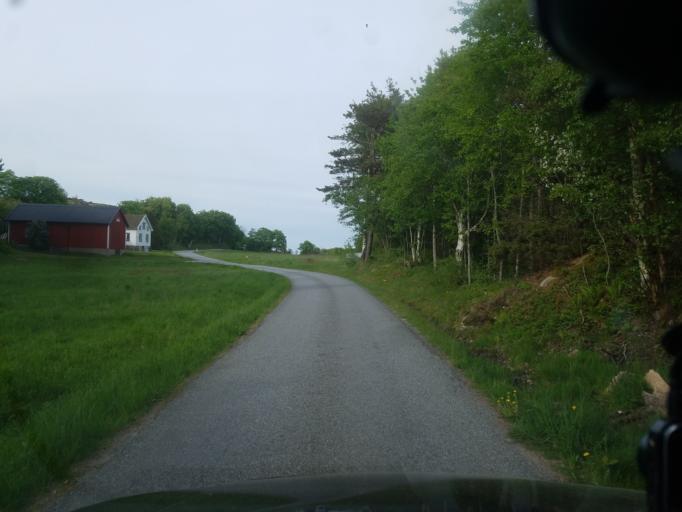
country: SE
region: Vaestra Goetaland
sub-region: Lysekils Kommun
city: Lysekil
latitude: 58.3000
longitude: 11.4503
